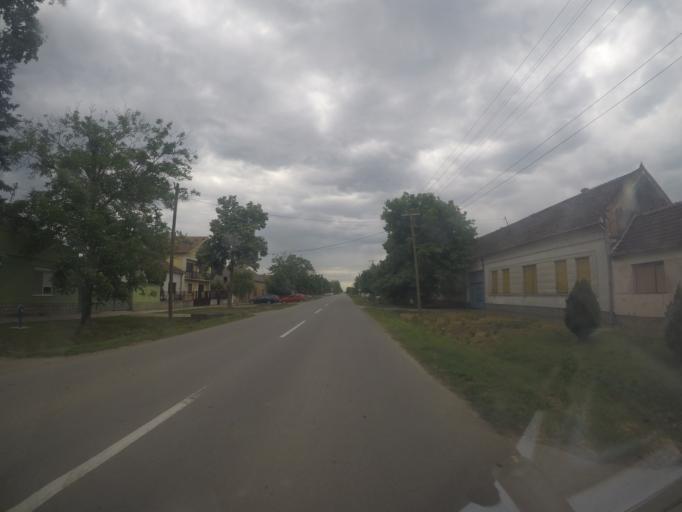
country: RS
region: Autonomna Pokrajina Vojvodina
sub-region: Juznobanatski Okrug
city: Opovo
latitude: 45.0483
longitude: 20.4320
